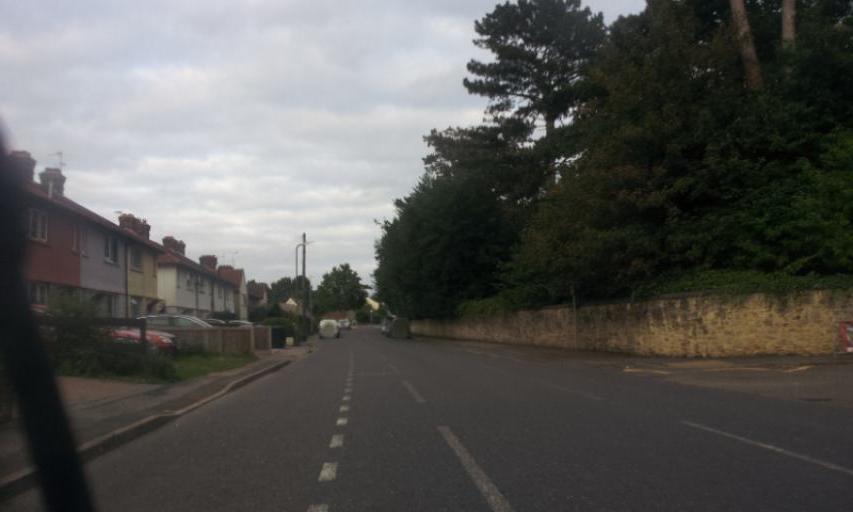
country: GB
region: England
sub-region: Kent
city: Maidstone
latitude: 51.2738
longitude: 0.4942
